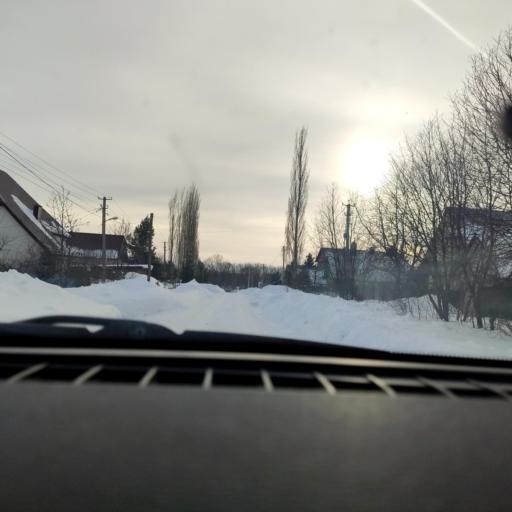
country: RU
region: Bashkortostan
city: Avdon
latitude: 54.6599
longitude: 55.7682
